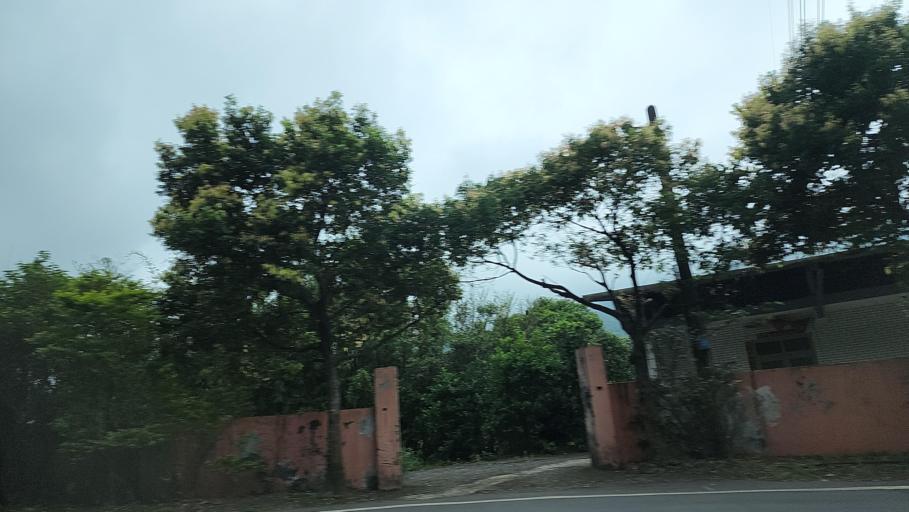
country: TW
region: Taiwan
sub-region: Keelung
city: Keelung
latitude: 25.1676
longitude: 121.6798
